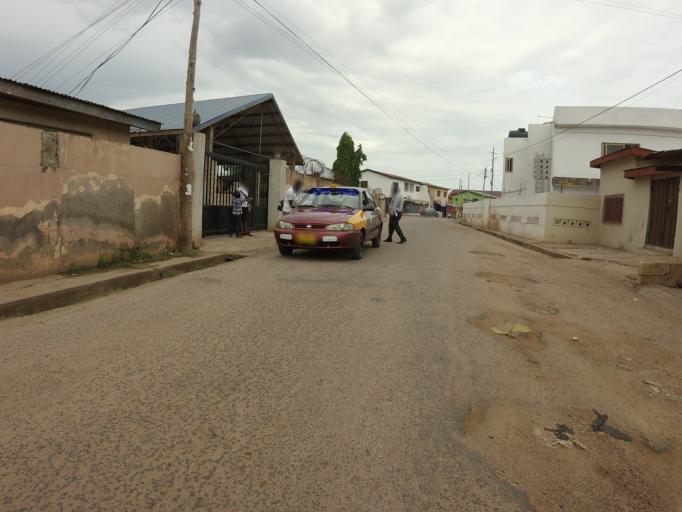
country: GH
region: Greater Accra
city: Accra
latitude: 5.6009
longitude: -0.2157
